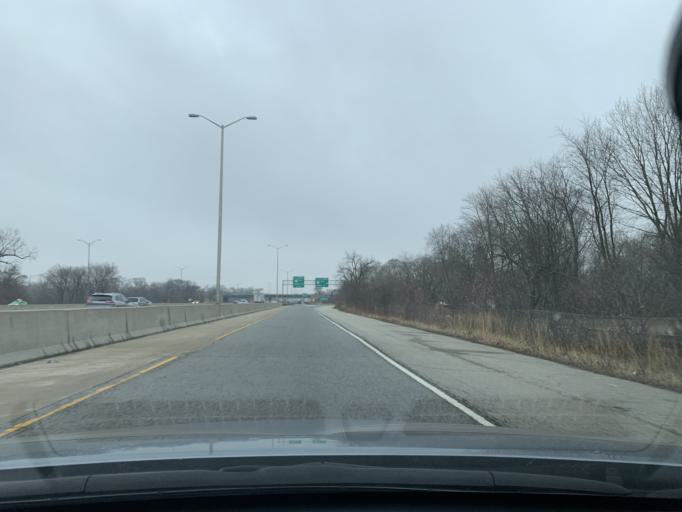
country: US
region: Illinois
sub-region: Cook County
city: Markham
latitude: 41.6048
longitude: -87.7055
